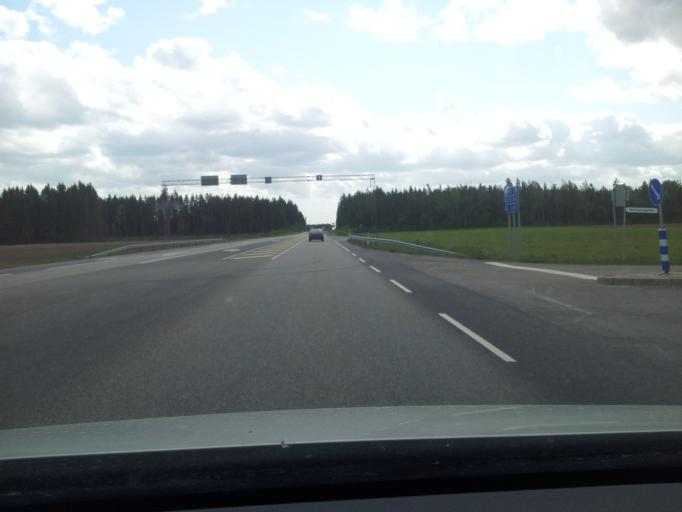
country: FI
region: Kymenlaakso
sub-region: Kouvola
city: Elimaeki
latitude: 60.7920
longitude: 26.5024
